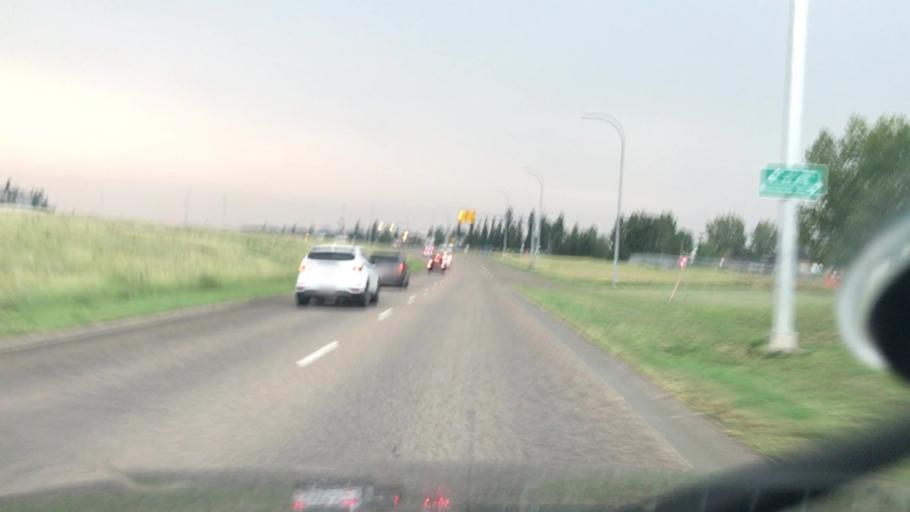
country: CA
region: Alberta
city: Edmonton
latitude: 53.4598
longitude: -113.5888
